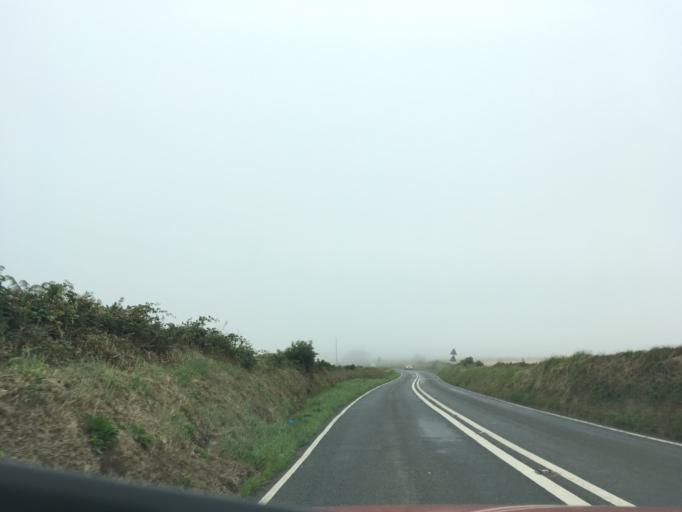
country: GB
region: Wales
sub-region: Pembrokeshire
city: Saint David's
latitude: 51.8799
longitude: -5.2459
